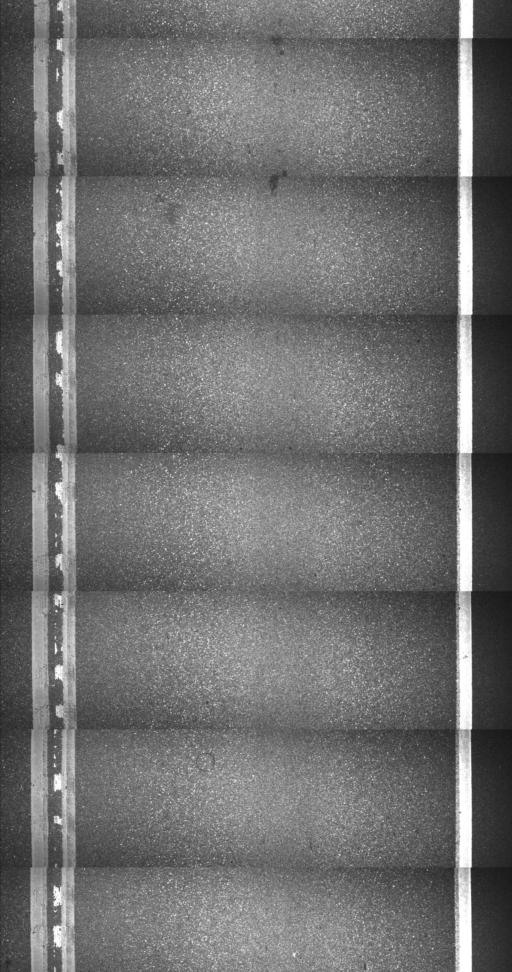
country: US
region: Vermont
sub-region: Orange County
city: Randolph
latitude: 43.7598
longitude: -72.7394
